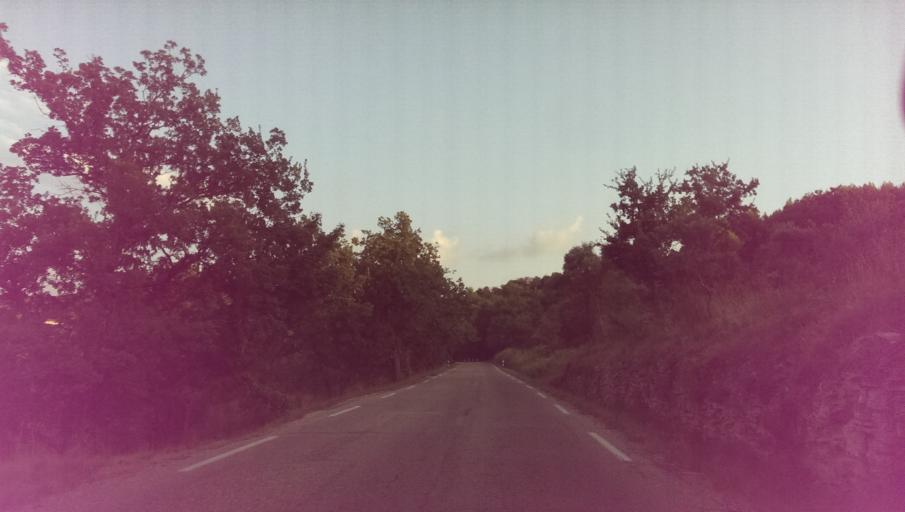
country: FR
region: Provence-Alpes-Cote d'Azur
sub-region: Departement du Vaucluse
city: Venasque
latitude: 43.9941
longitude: 5.1591
